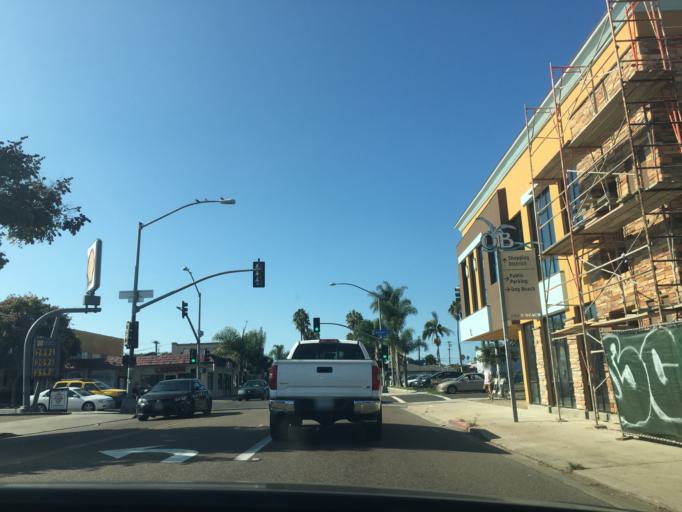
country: US
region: California
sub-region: San Diego County
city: Coronado
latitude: 32.7503
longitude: -117.2429
